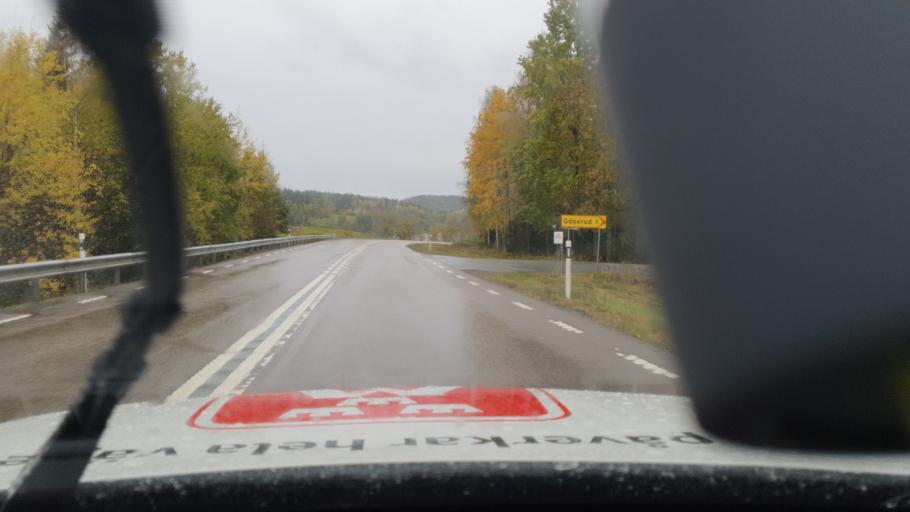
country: SE
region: Vaestra Goetaland
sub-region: Dals-Ed Kommun
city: Ed
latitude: 58.9274
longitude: 12.0358
